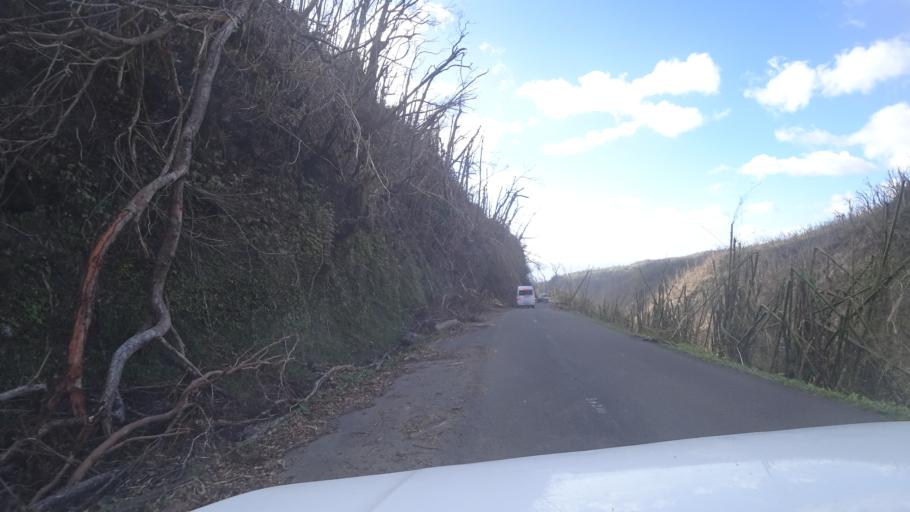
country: DM
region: Saint Luke
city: Pointe Michel
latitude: 15.2702
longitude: -61.3510
